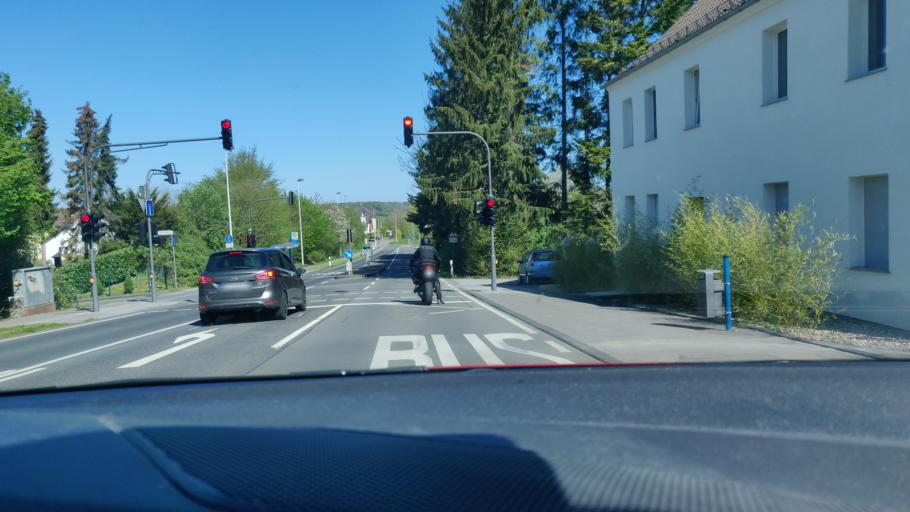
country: DE
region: North Rhine-Westphalia
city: Wulfrath
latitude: 51.2653
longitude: 7.0734
